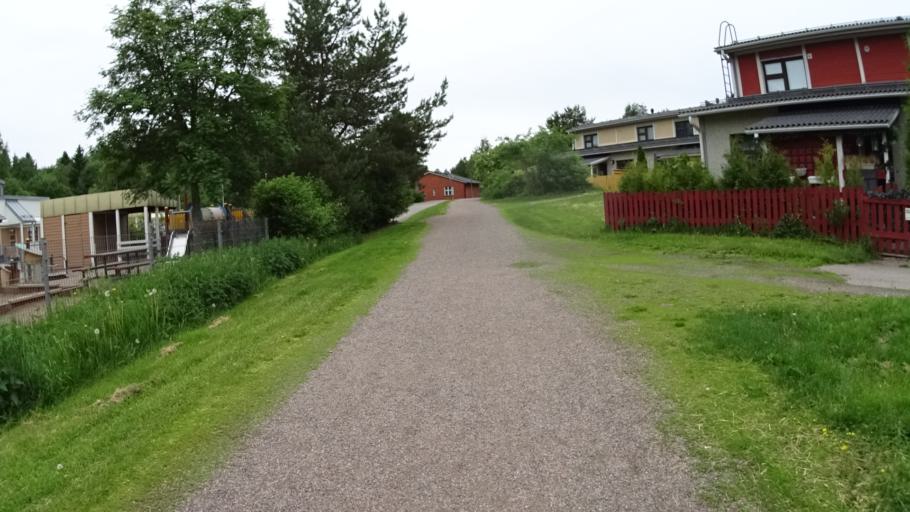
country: FI
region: Uusimaa
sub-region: Helsinki
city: Kilo
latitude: 60.2727
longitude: 24.8163
